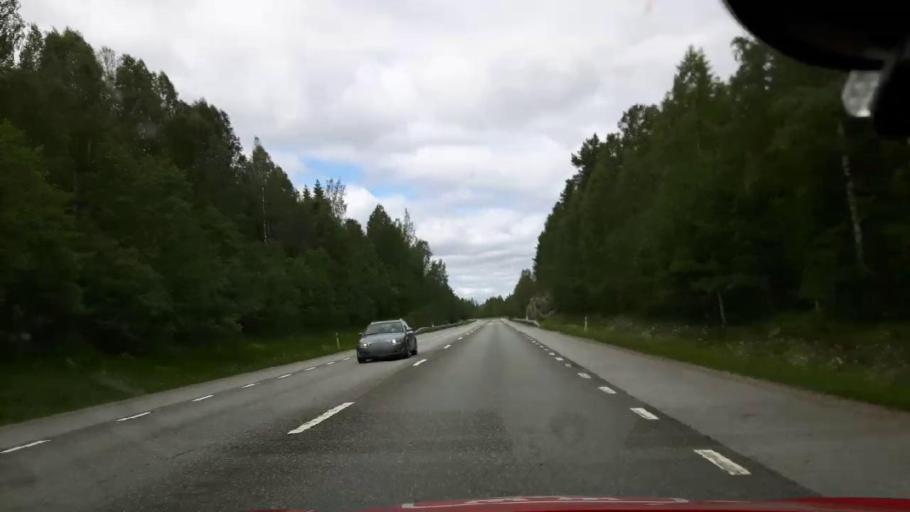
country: SE
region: Jaemtland
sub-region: Braecke Kommun
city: Braecke
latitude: 62.6977
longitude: 15.5258
